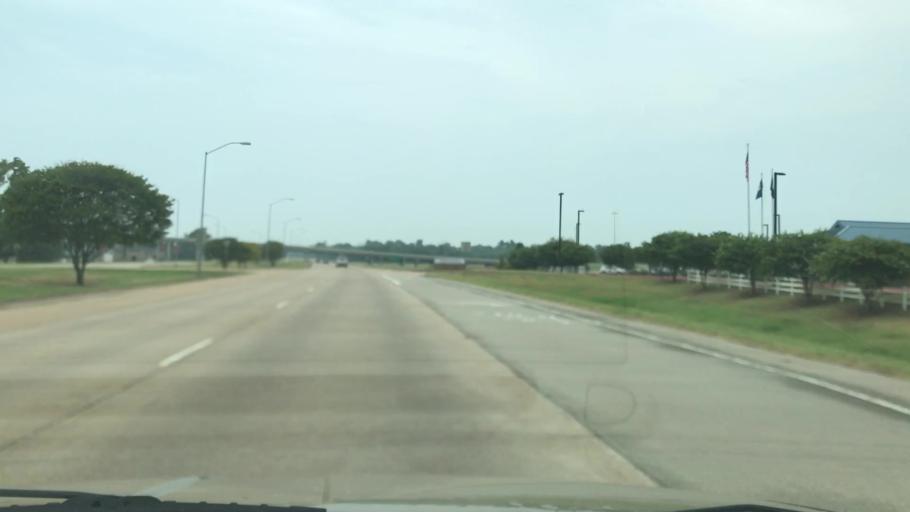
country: US
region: Louisiana
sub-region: Bossier Parish
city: Bossier City
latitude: 32.4911
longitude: -93.6925
